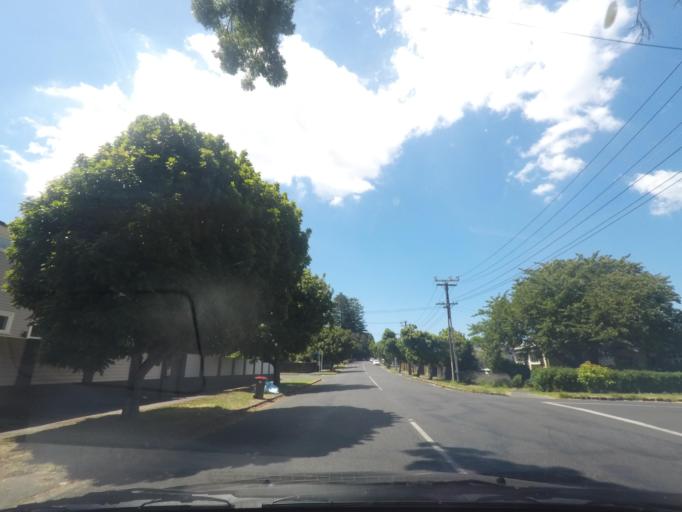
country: NZ
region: Auckland
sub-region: Auckland
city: Auckland
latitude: -36.9051
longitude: 174.7649
